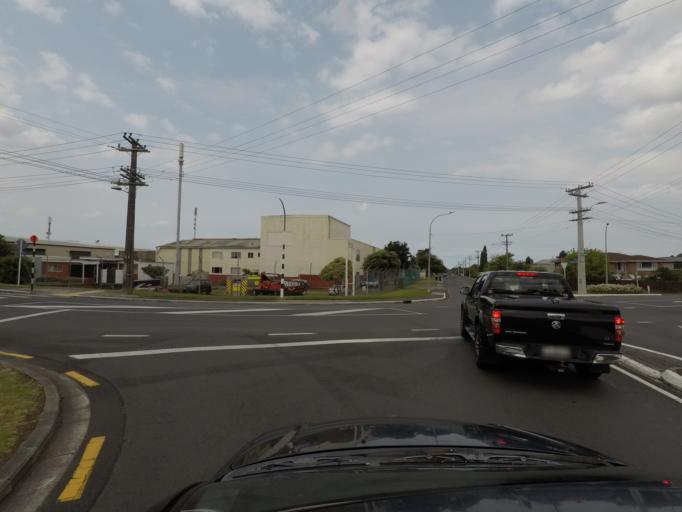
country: NZ
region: Auckland
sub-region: Auckland
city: Rosebank
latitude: -36.8316
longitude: 174.6466
